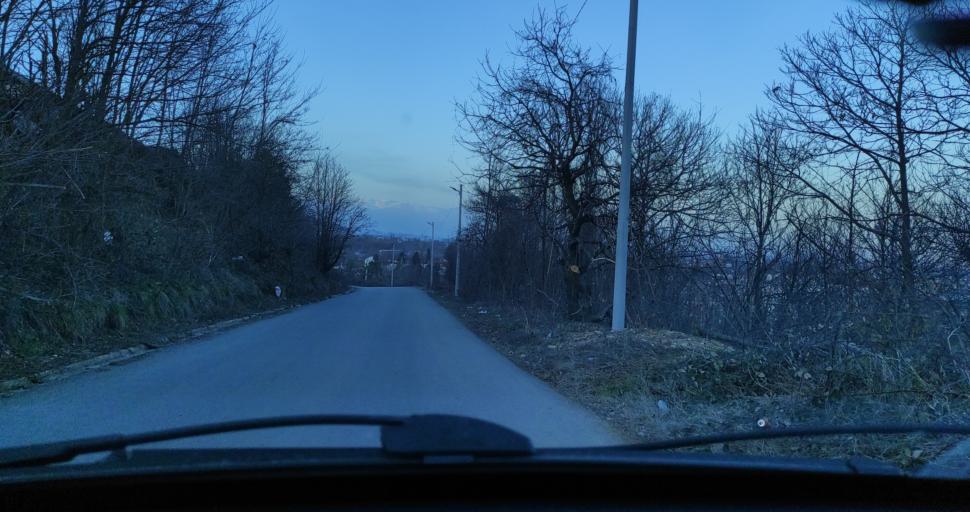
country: XK
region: Gjakova
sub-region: Komuna e Decanit
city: Decan
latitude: 42.5384
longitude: 20.2842
